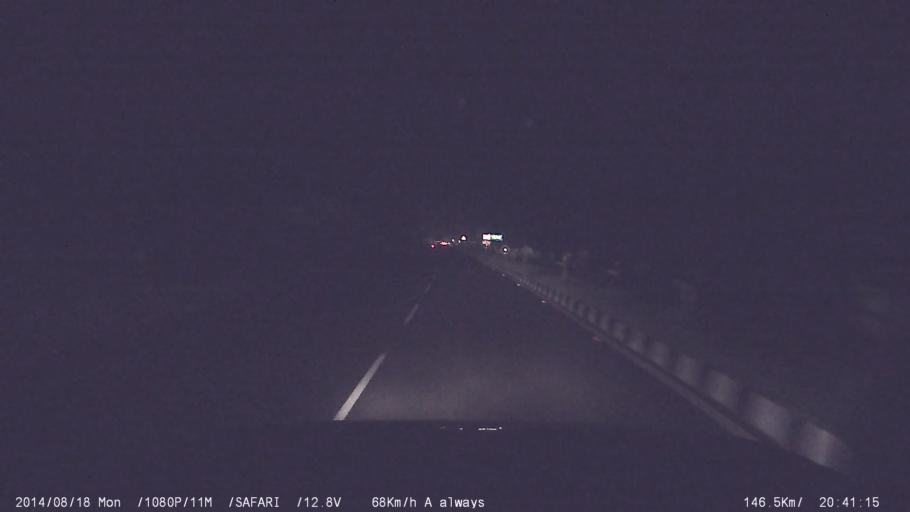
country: IN
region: Kerala
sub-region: Thrissur District
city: Kizhake Chalakudi
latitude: 10.3420
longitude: 76.3223
